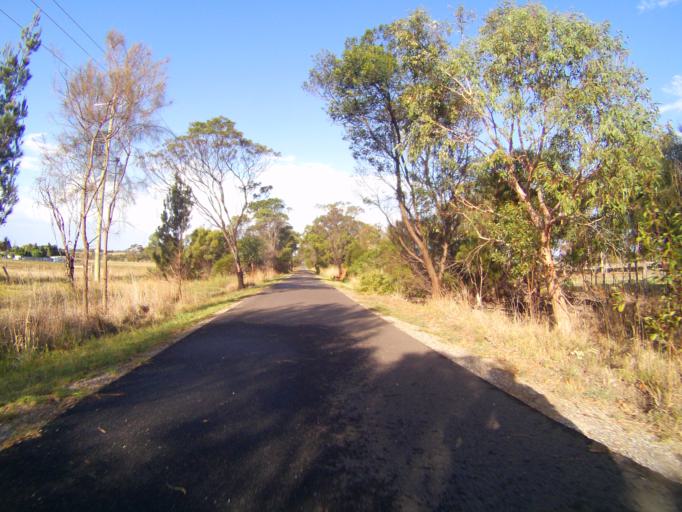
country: AU
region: Victoria
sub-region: Greater Geelong
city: Leopold
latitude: -38.1820
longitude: 144.4998
